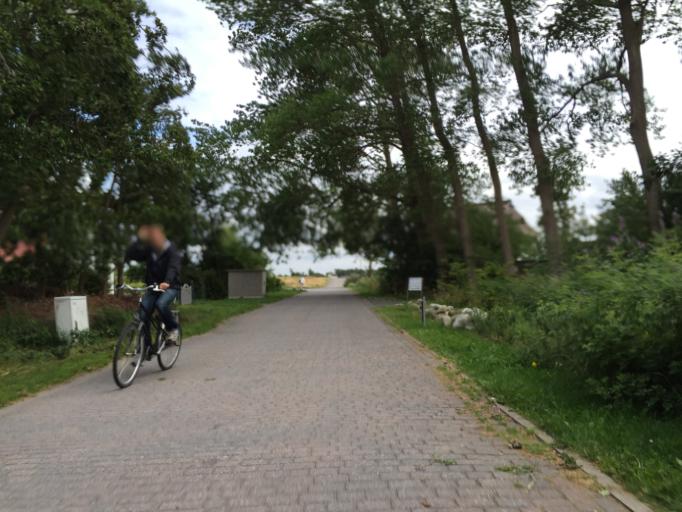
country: DE
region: Mecklenburg-Vorpommern
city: Hiddensee
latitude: 54.5615
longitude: 13.1034
